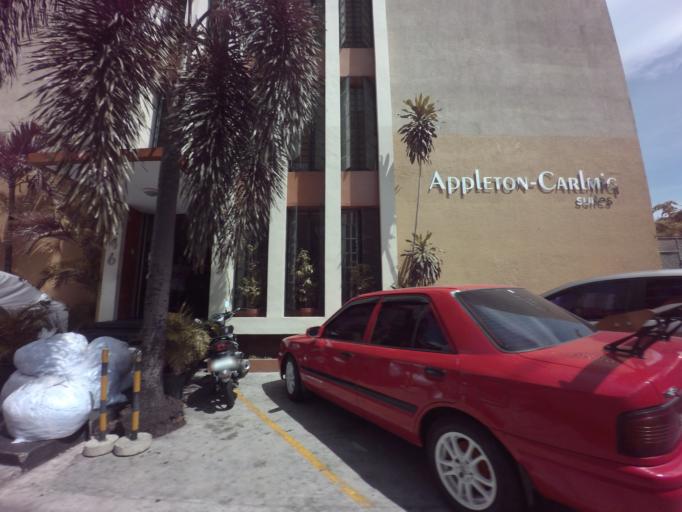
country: PH
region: Metro Manila
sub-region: Makati City
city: Makati City
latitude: 14.5527
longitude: 120.9960
